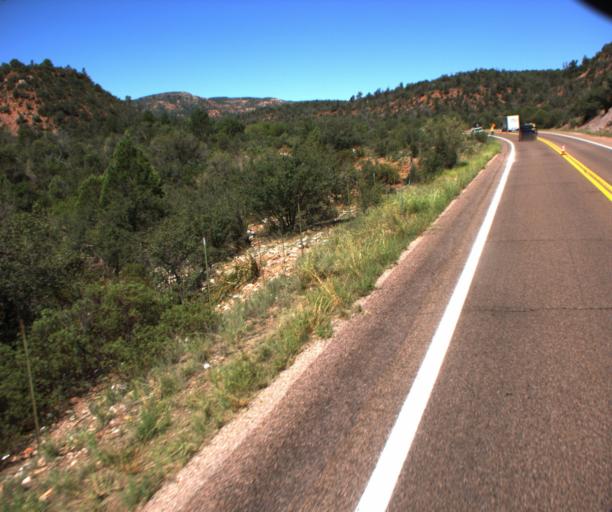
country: US
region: Arizona
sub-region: Navajo County
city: Cibecue
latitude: 33.9823
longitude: -110.2965
